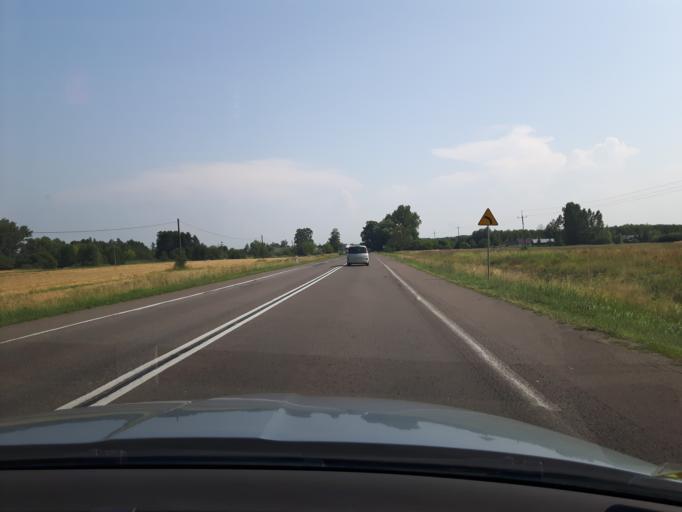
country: PL
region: Masovian Voivodeship
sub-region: Powiat ciechanowski
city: Glinojeck
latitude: 52.7718
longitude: 20.2935
